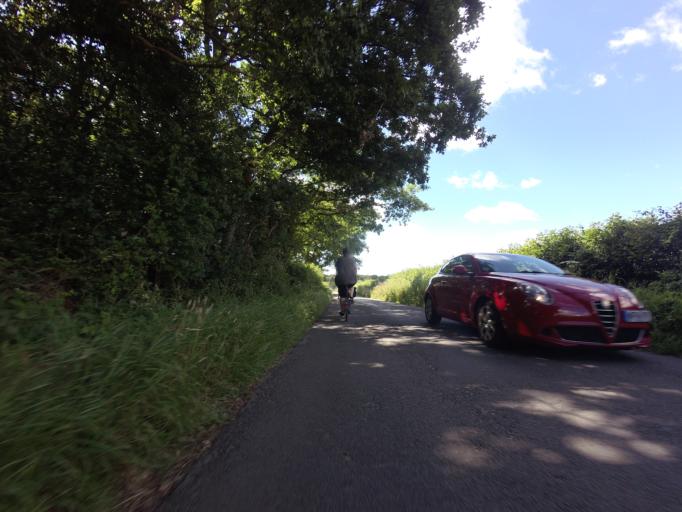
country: GB
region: England
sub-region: East Sussex
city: Horam
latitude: 50.9048
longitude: 0.1930
